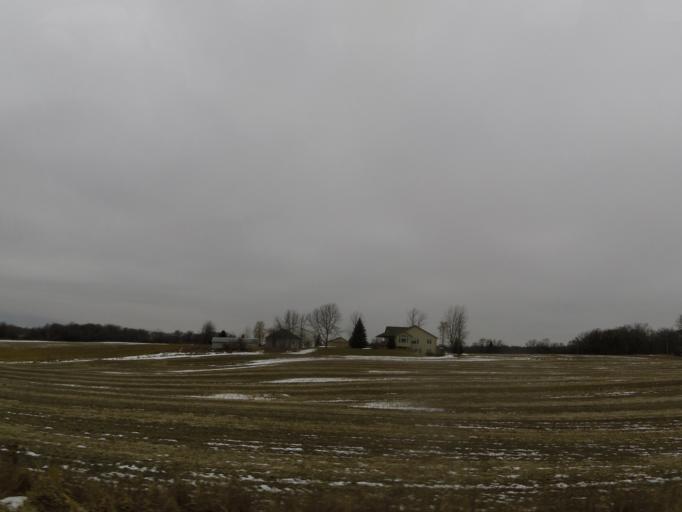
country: US
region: Minnesota
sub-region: Carver County
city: Watertown
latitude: 44.9913
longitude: -93.8488
